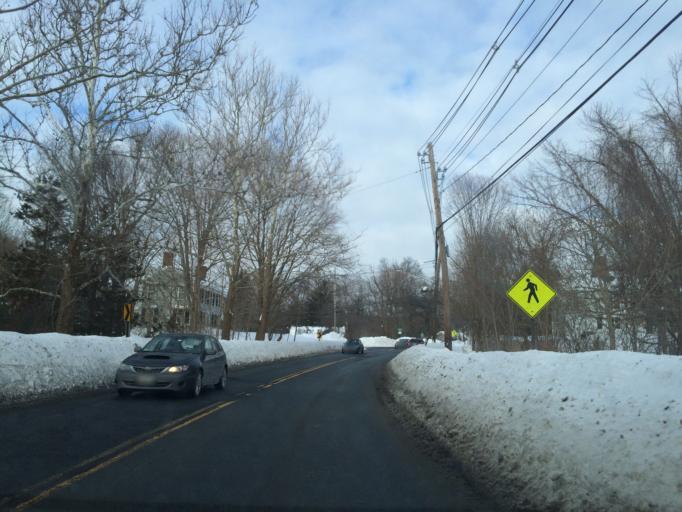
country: US
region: Massachusetts
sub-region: Middlesex County
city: Weston
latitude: 42.3798
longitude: -71.2805
